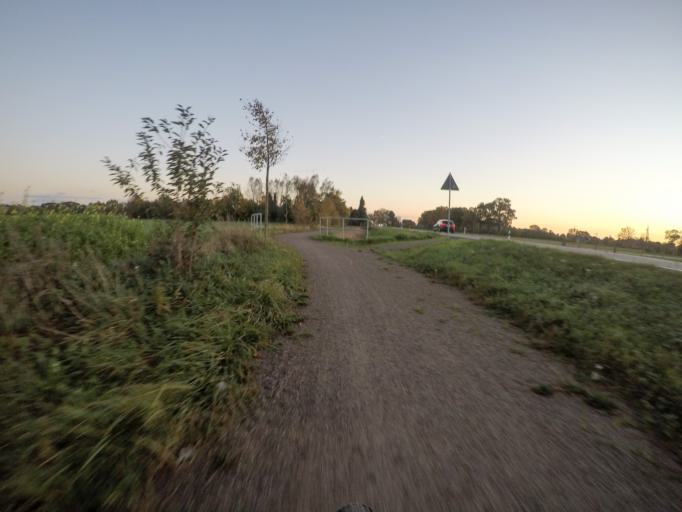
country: DE
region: North Rhine-Westphalia
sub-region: Regierungsbezirk Dusseldorf
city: Bocholt
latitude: 51.8376
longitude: 6.5566
